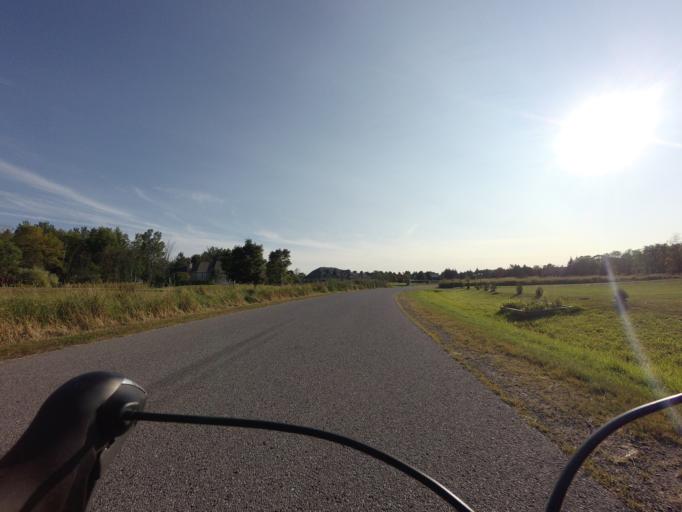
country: CA
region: Ontario
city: Bells Corners
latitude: 45.4470
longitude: -75.9887
